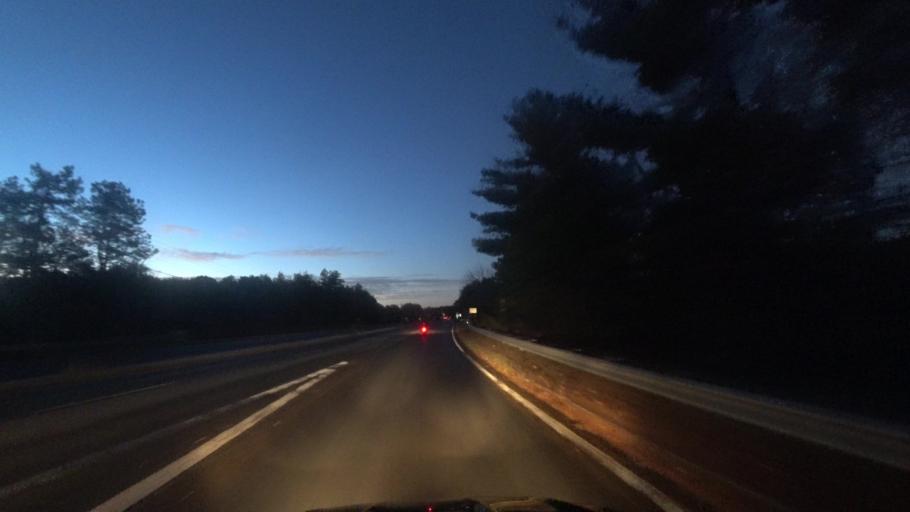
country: US
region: Massachusetts
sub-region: Essex County
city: Andover
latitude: 42.6064
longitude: -71.1228
